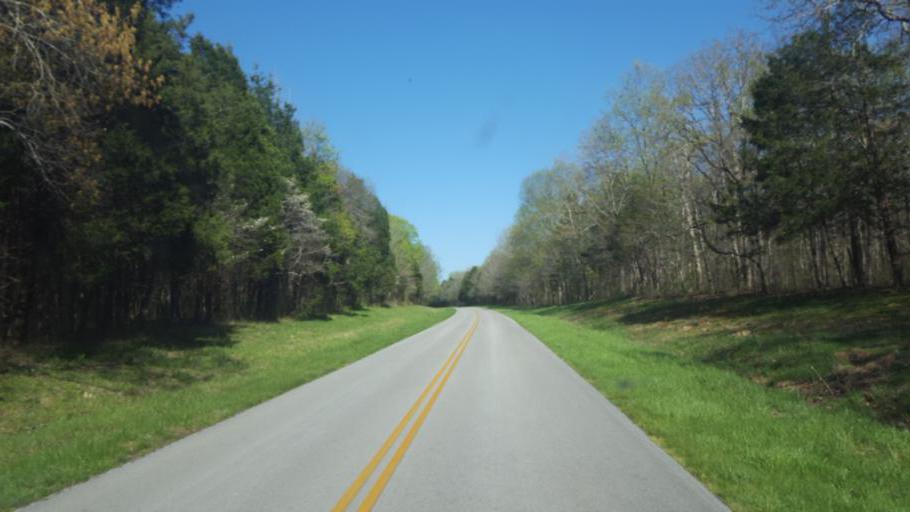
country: US
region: Kentucky
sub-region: Edmonson County
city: Brownsville
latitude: 37.1599
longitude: -86.1471
